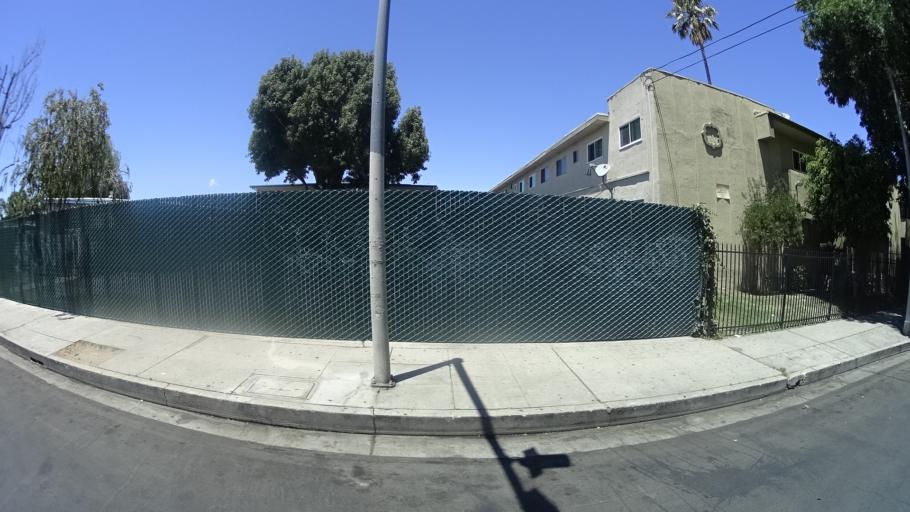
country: US
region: California
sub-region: Los Angeles County
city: Van Nuys
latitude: 34.2312
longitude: -118.4697
